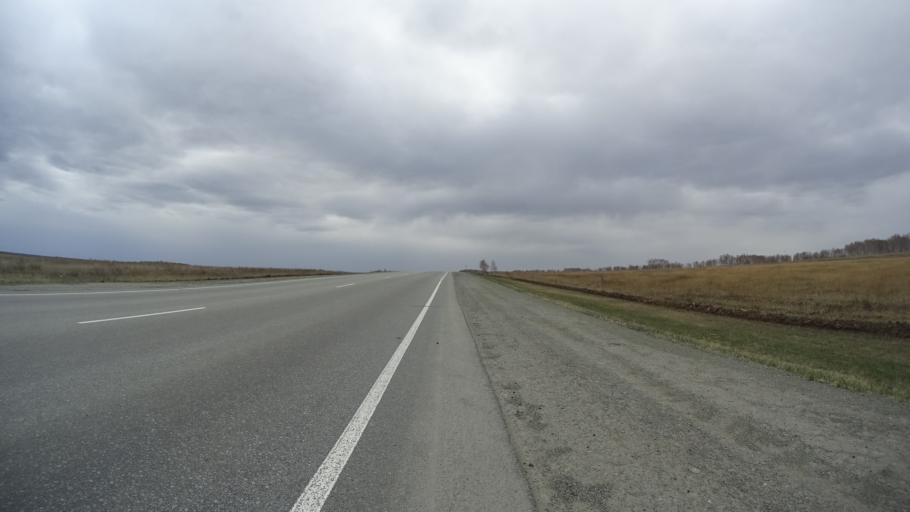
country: RU
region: Chelyabinsk
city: Yemanzhelinsk
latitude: 54.7080
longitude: 61.2581
